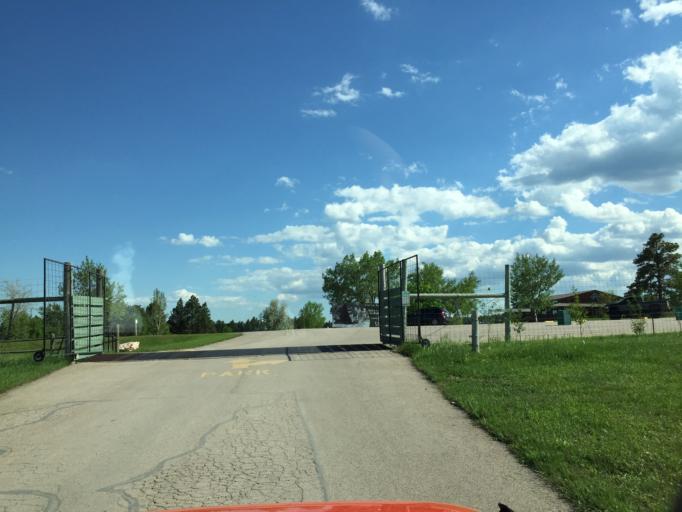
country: US
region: South Dakota
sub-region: Pennington County
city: Colonial Pine Hills
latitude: 43.9770
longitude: -103.3009
